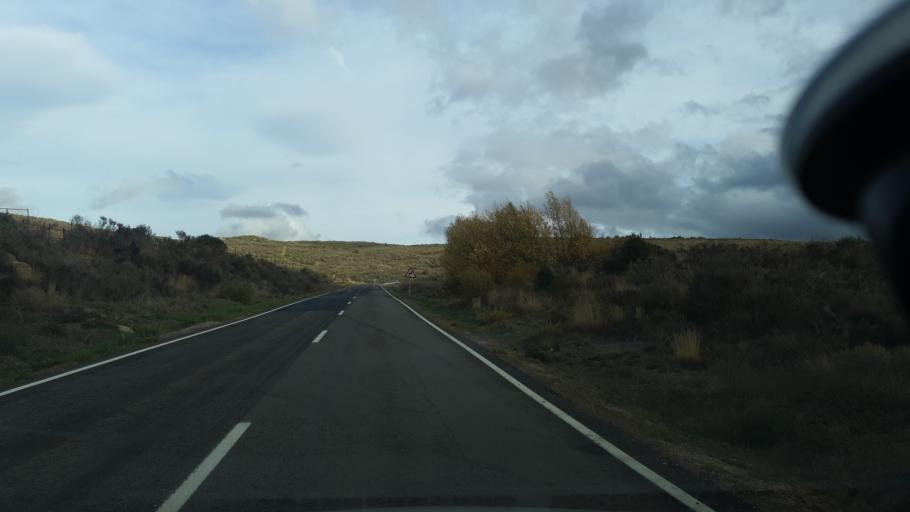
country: ES
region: Castille and Leon
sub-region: Provincia de Avila
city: San Martin del Pimpollar
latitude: 40.3914
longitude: -5.0194
